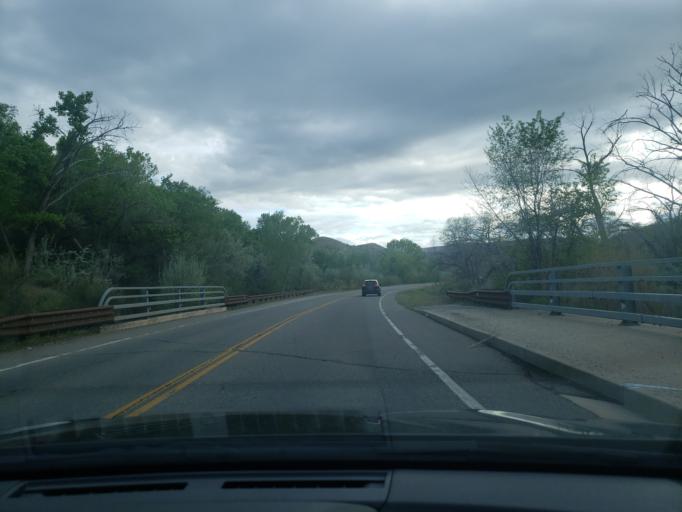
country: US
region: Colorado
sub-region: Mesa County
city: Grand Junction
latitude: 39.0591
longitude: -108.5900
